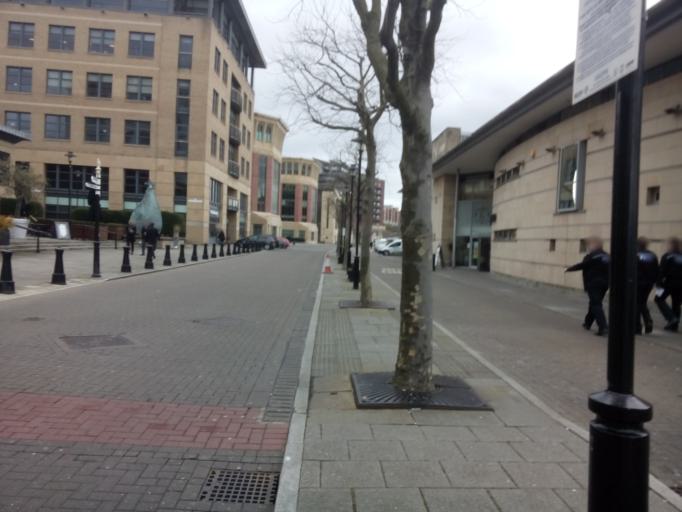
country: GB
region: England
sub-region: Gateshead
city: Gateshead
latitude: 54.9705
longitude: -1.6000
